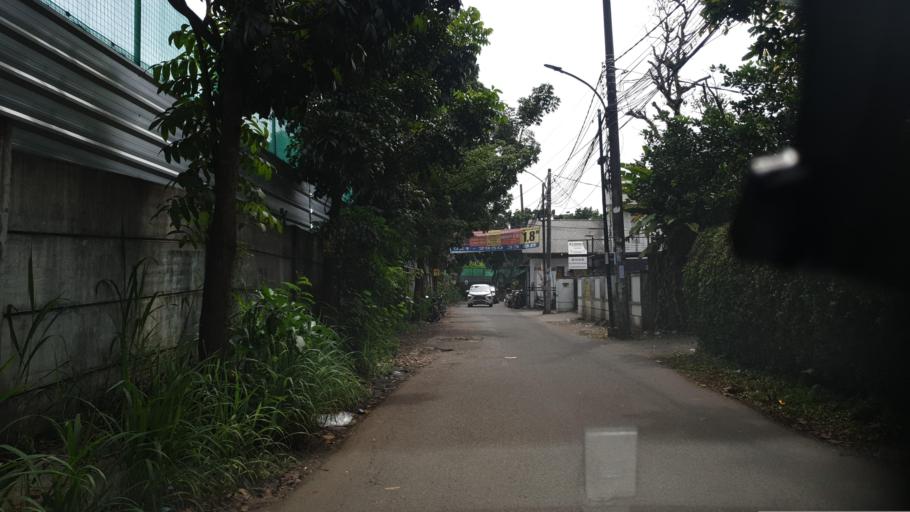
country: ID
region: West Java
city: Pamulang
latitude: -6.3475
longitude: 106.7701
